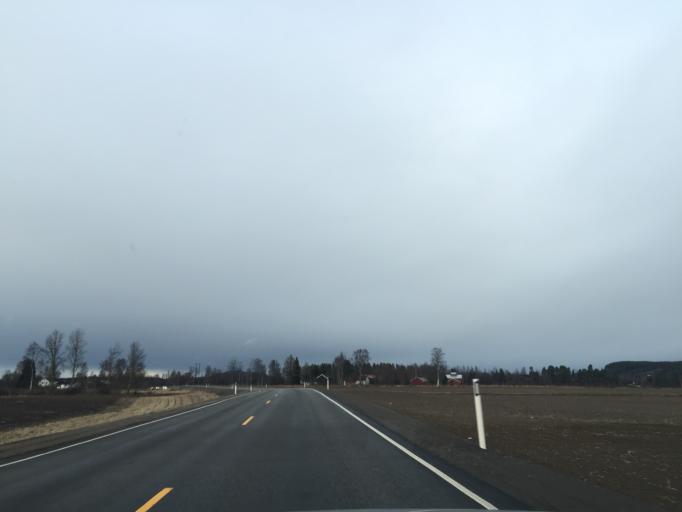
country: NO
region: Hedmark
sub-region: Grue
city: Kirkenaer
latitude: 60.5335
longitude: 12.0623
